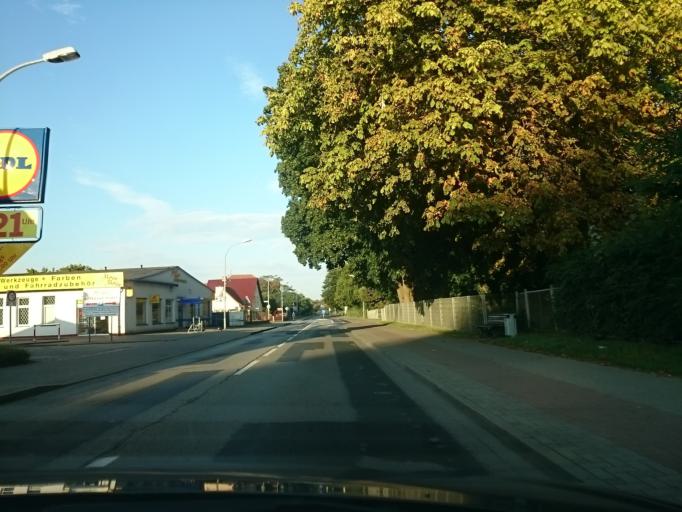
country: DE
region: Mecklenburg-Vorpommern
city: Wolgast
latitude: 54.0512
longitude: 13.7674
